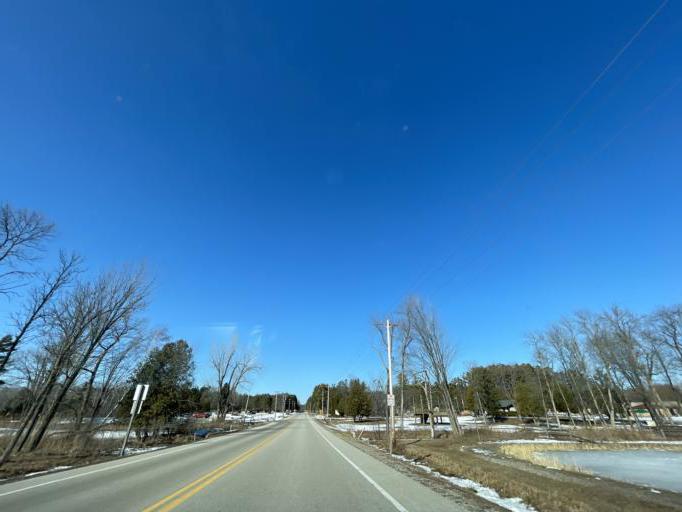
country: US
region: Wisconsin
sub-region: Brown County
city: Suamico
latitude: 44.6592
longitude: -88.0903
